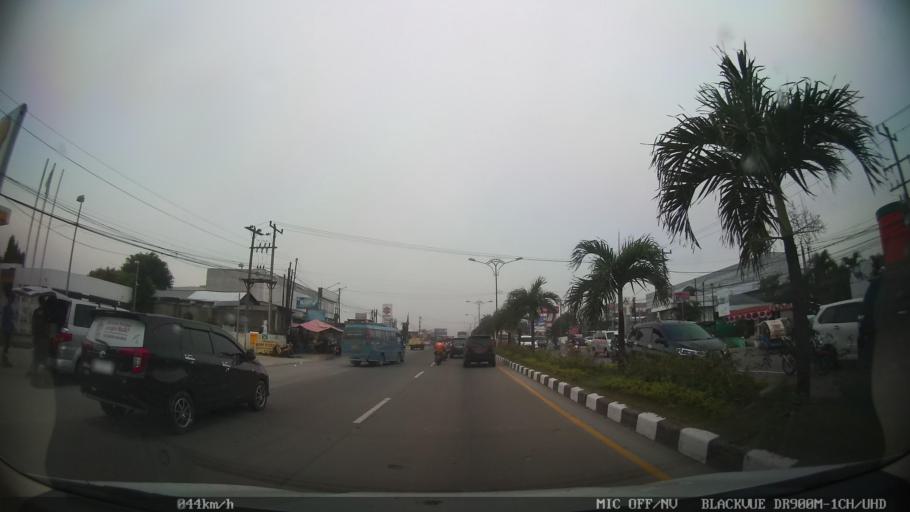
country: ID
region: North Sumatra
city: Deli Tua
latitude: 3.5379
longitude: 98.7079
